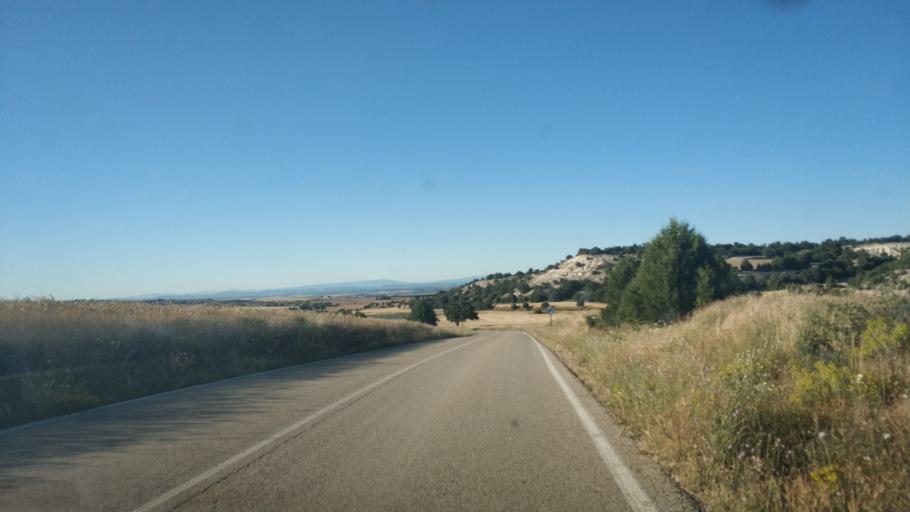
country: ES
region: Castille and Leon
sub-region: Provincia de Soria
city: Liceras
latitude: 41.4689
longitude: -3.2172
